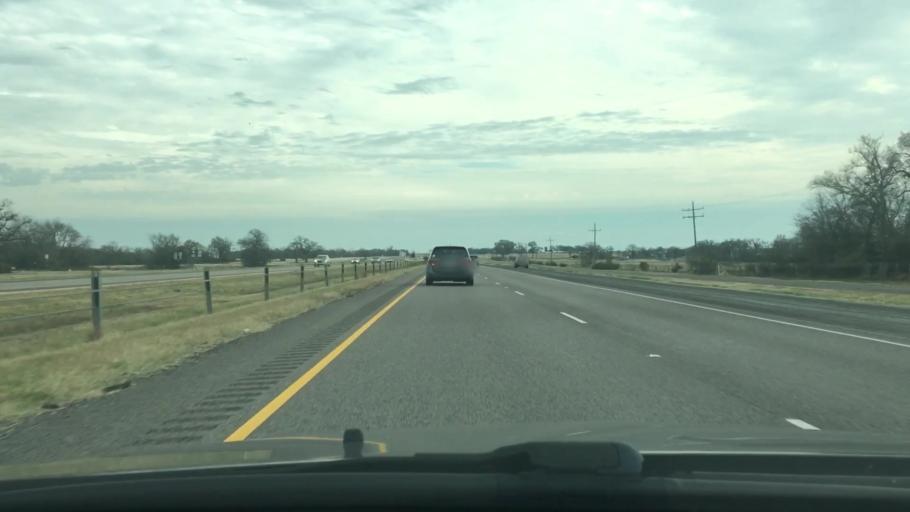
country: US
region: Texas
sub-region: Madison County
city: Madisonville
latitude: 31.0032
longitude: -95.9149
